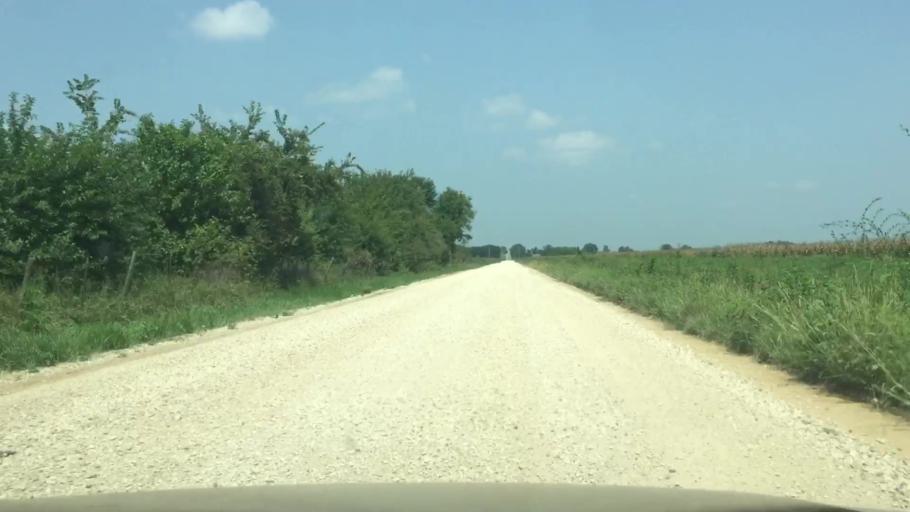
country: US
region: Kansas
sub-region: Allen County
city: Iola
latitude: 37.8701
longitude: -95.3911
